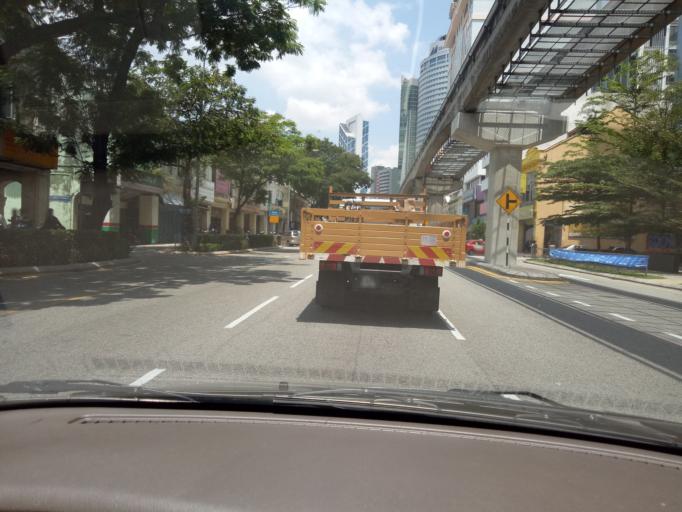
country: MY
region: Kuala Lumpur
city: Kuala Lumpur
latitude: 3.1619
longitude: 101.6977
